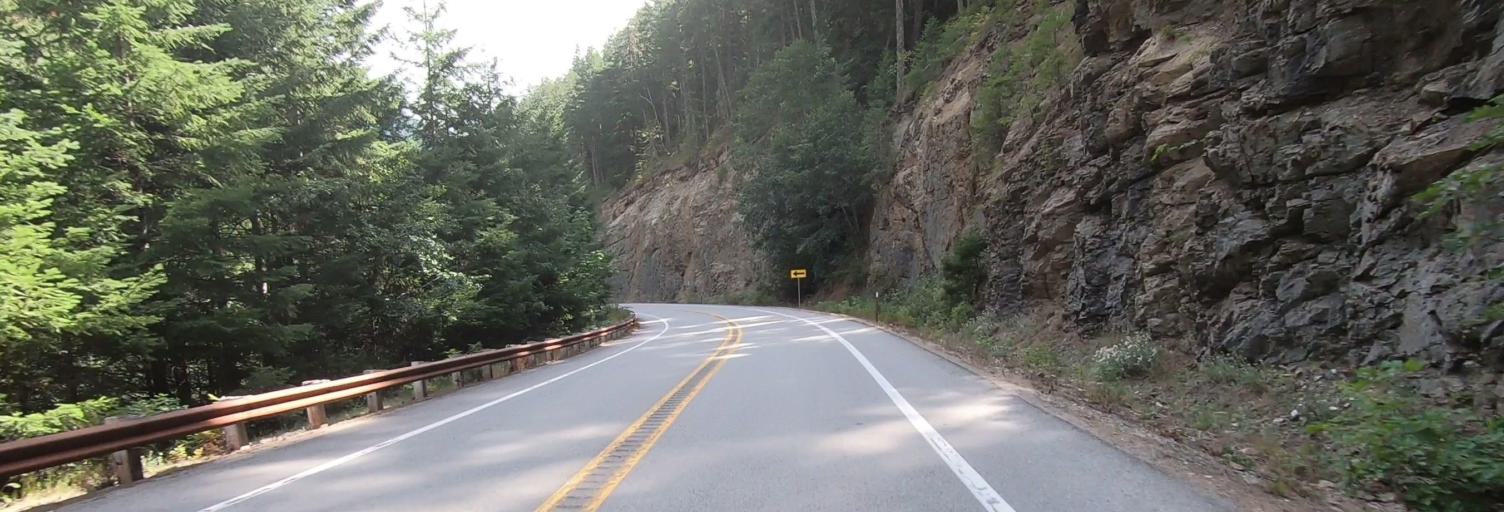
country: US
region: Washington
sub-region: Snohomish County
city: Darrington
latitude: 48.6910
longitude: -120.9119
